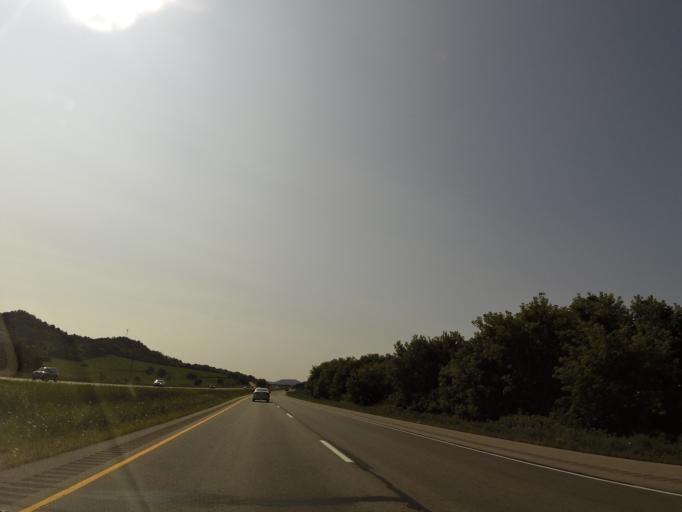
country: US
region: Wisconsin
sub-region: La Crosse County
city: West Salem
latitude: 43.8914
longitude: -91.0586
